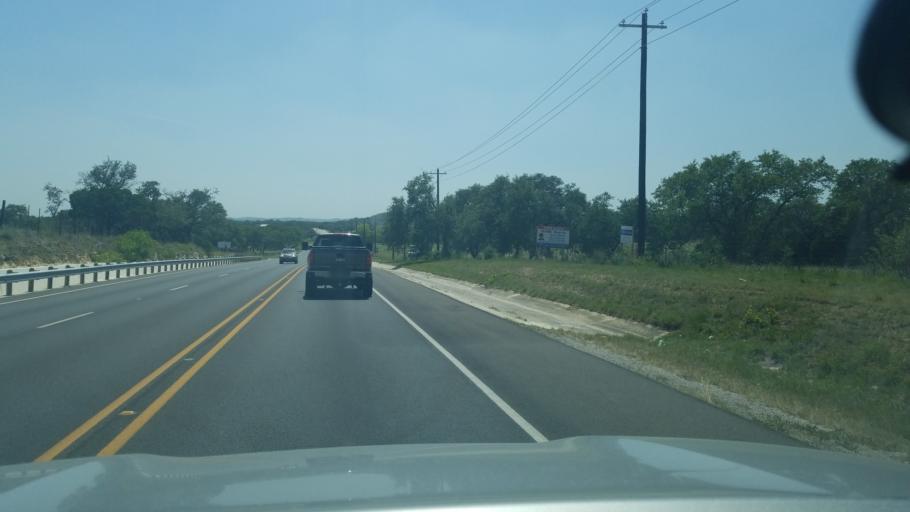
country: US
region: Texas
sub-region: Bexar County
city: Fair Oaks Ranch
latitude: 29.7964
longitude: -98.6702
